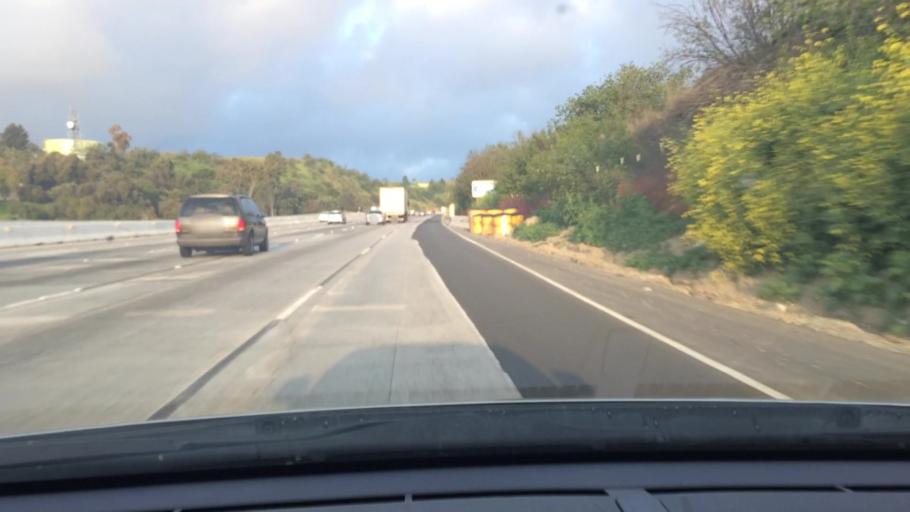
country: US
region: California
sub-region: Los Angeles County
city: Diamond Bar
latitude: 34.0641
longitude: -117.8207
